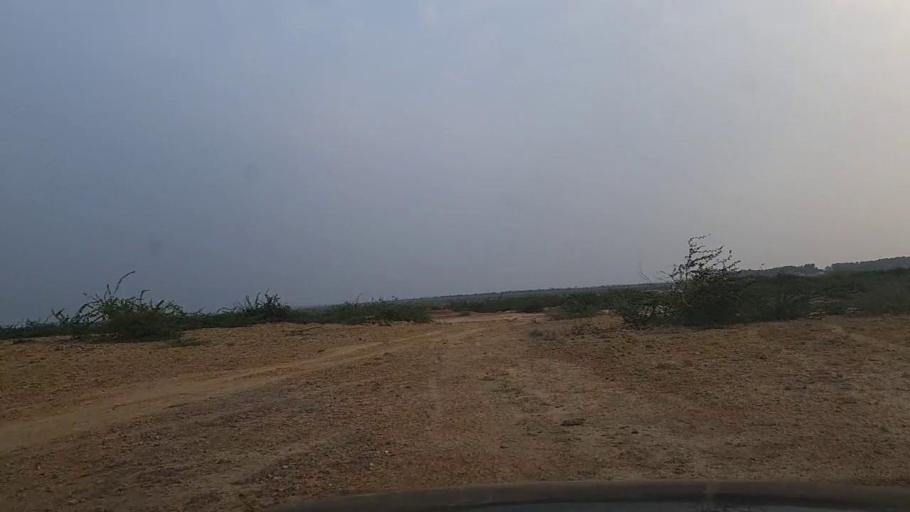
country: PK
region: Sindh
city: Gharo
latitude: 24.7701
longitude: 67.6922
